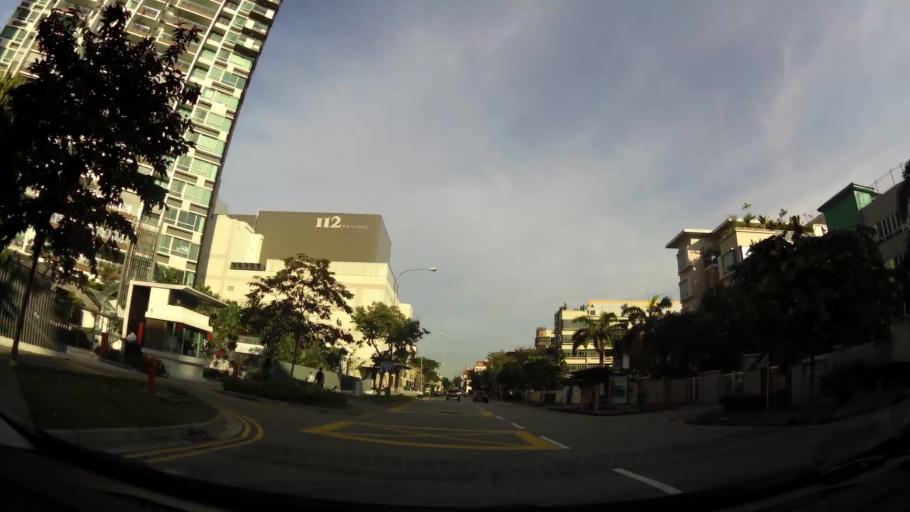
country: SG
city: Singapore
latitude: 1.3044
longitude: 103.9059
